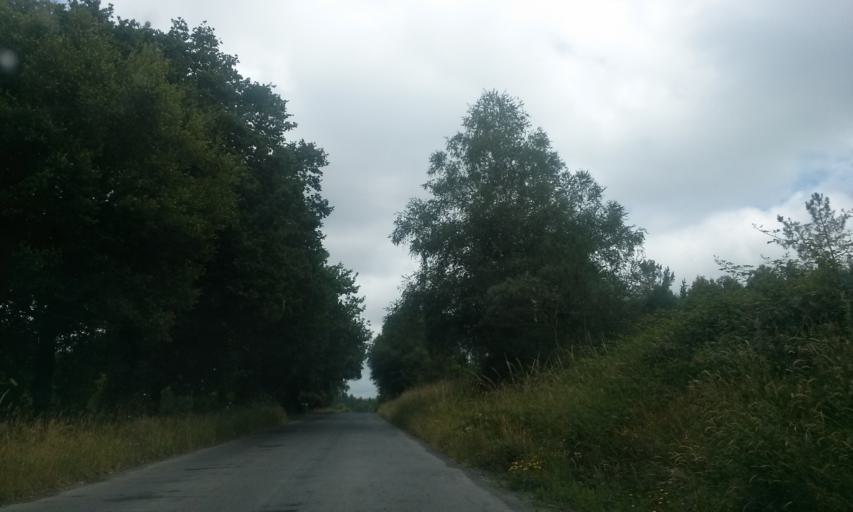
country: ES
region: Galicia
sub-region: Provincia de Lugo
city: Friol
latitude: 43.0838
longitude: -7.8136
